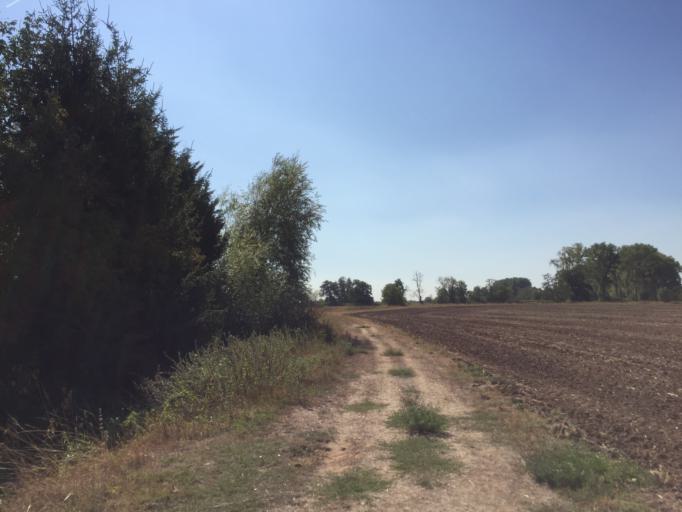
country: DE
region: Hesse
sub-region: Regierungsbezirk Giessen
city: Hungen
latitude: 50.4443
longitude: 8.9056
